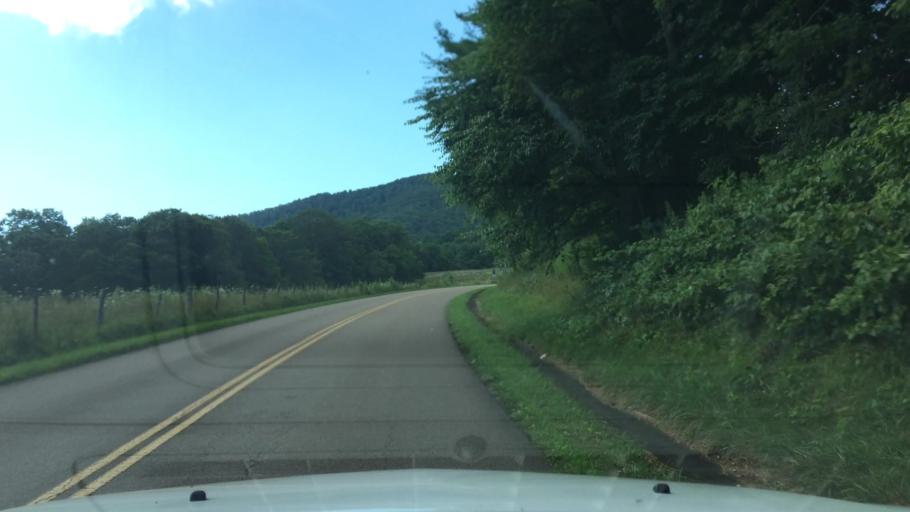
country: US
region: North Carolina
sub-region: Watauga County
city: Blowing Rock
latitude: 36.1497
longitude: -81.6653
